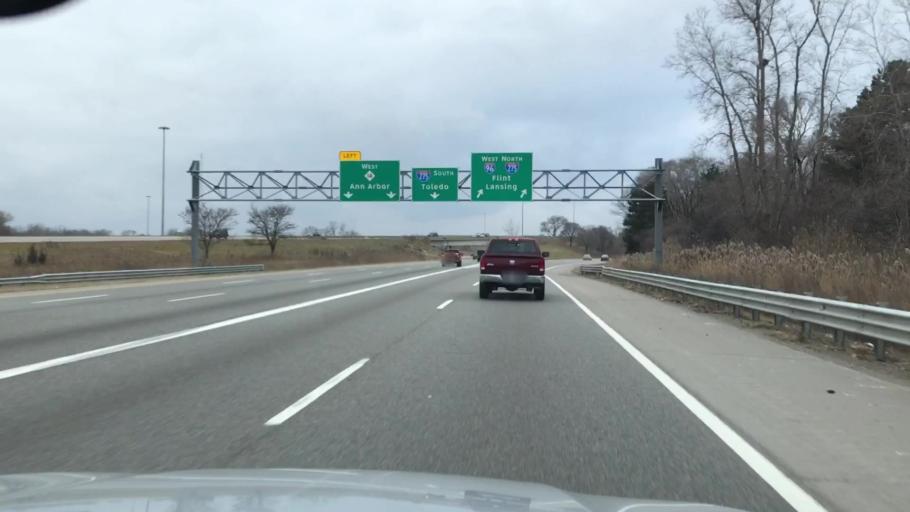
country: US
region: Michigan
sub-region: Wayne County
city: Plymouth
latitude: 42.3848
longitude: -83.4281
